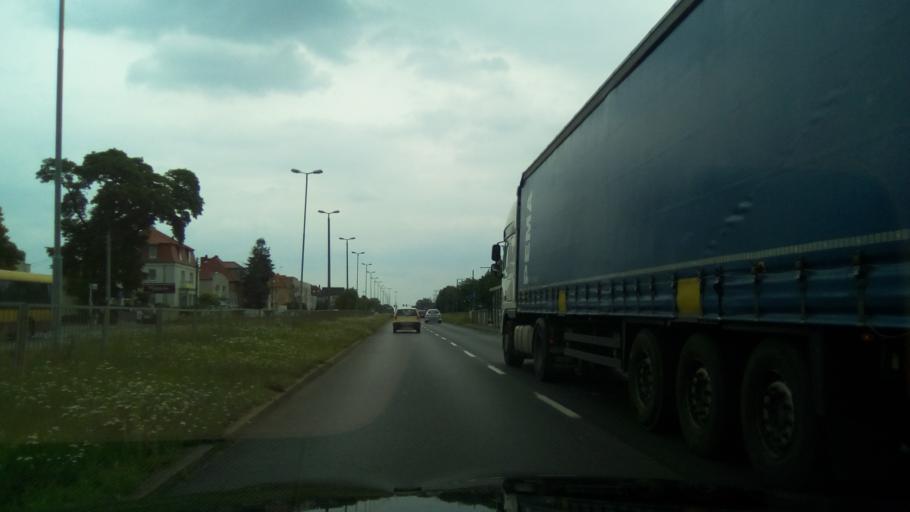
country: PL
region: Greater Poland Voivodeship
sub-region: Poznan
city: Poznan
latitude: 52.4097
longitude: 16.9845
